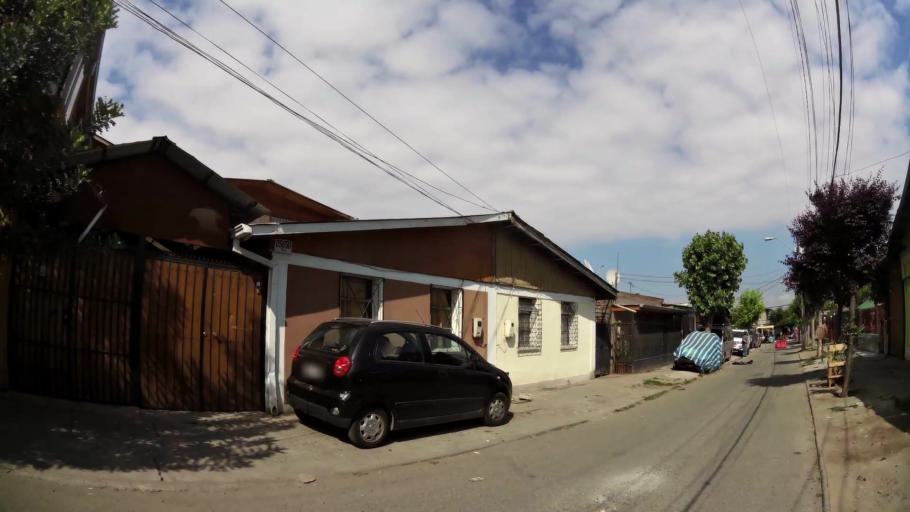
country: CL
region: Santiago Metropolitan
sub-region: Provincia de Maipo
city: San Bernardo
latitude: -33.5184
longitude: -70.6967
